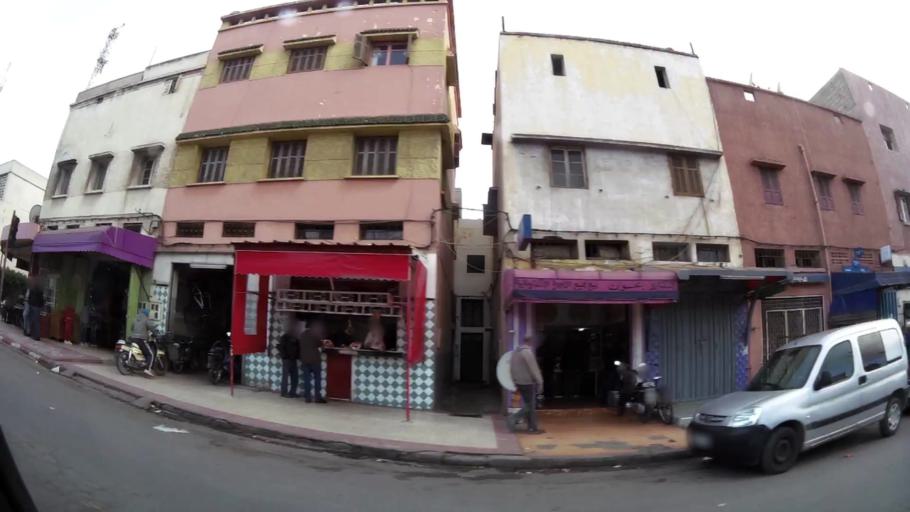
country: MA
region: Grand Casablanca
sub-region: Mohammedia
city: Mohammedia
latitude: 33.6875
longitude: -7.3913
